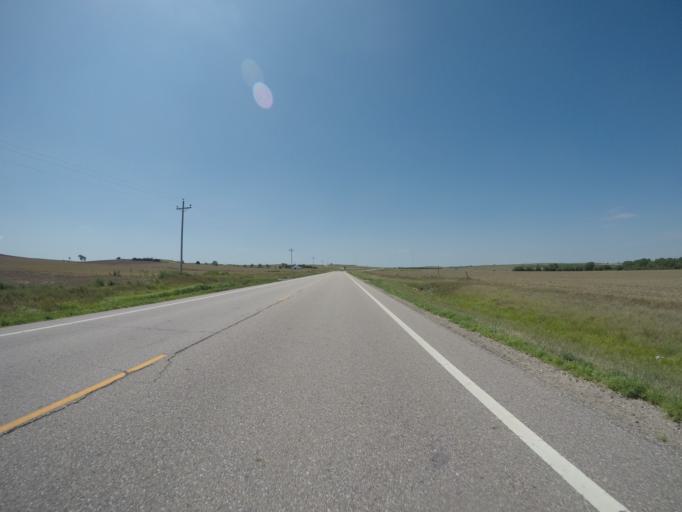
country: US
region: Kansas
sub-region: Osborne County
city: Osborne
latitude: 39.5031
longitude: -98.6935
